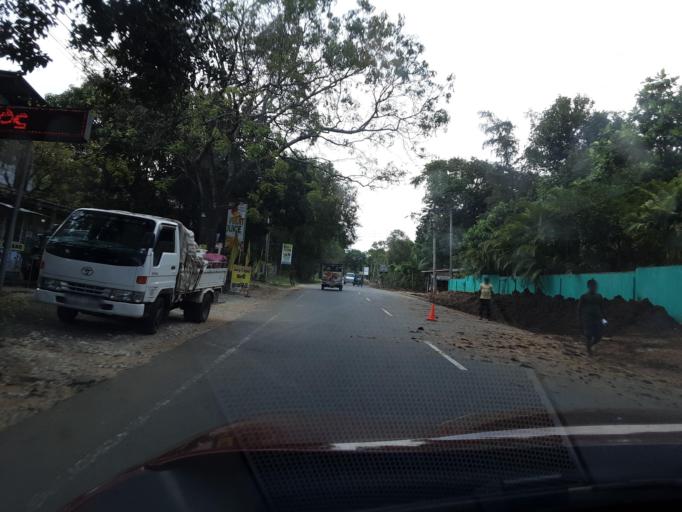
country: LK
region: Uva
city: Haputale
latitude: 6.6829
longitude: 81.1093
